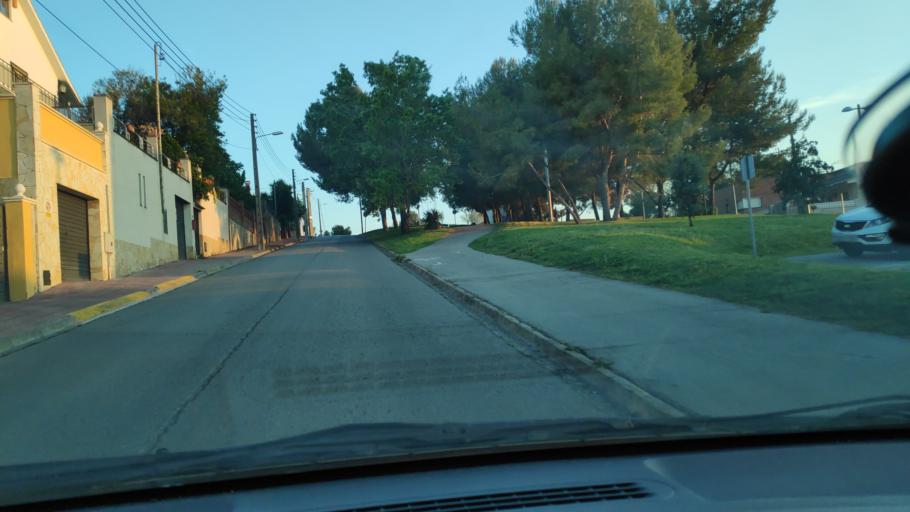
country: ES
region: Catalonia
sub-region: Provincia de Barcelona
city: Sant Quirze del Valles
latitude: 41.5331
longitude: 2.0483
